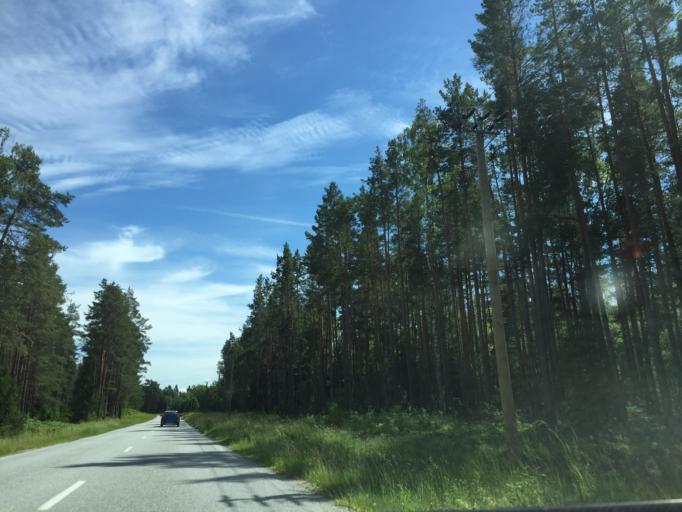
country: LV
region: Talsu Rajons
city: Valdemarpils
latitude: 57.5925
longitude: 22.6081
